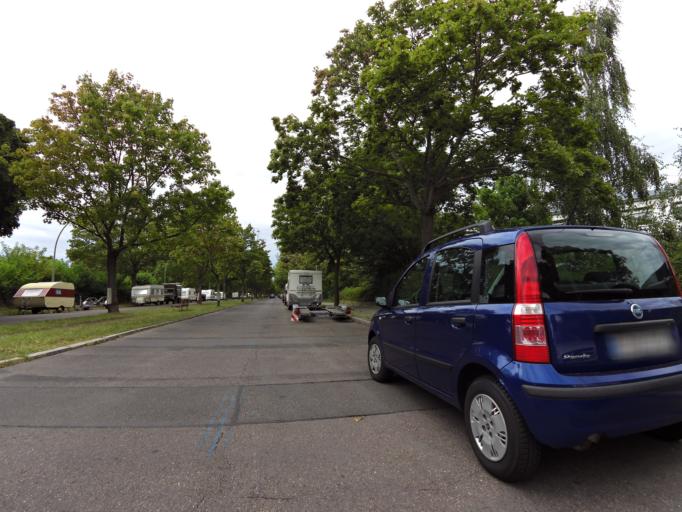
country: DE
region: Berlin
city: Schmargendorf
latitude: 52.4682
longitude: 13.3034
